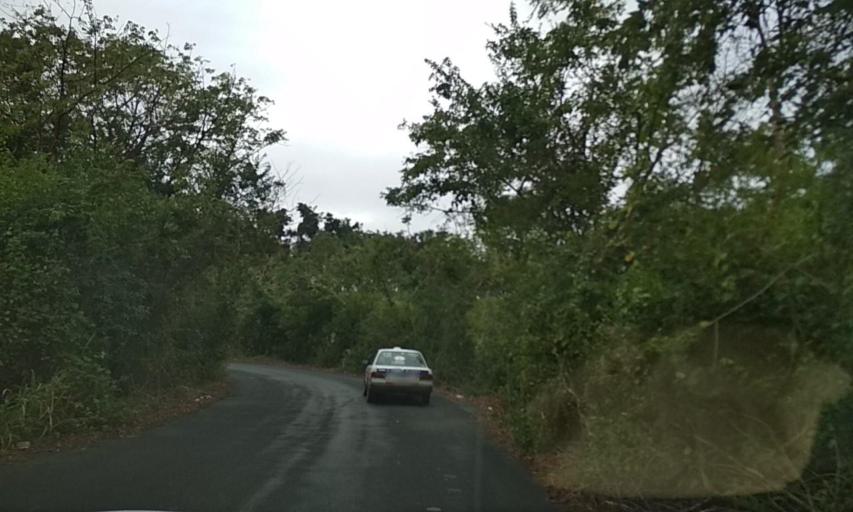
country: MX
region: Veracruz
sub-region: Coatzintla
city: Manuel Maria Contreras
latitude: 20.4474
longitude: -97.4992
